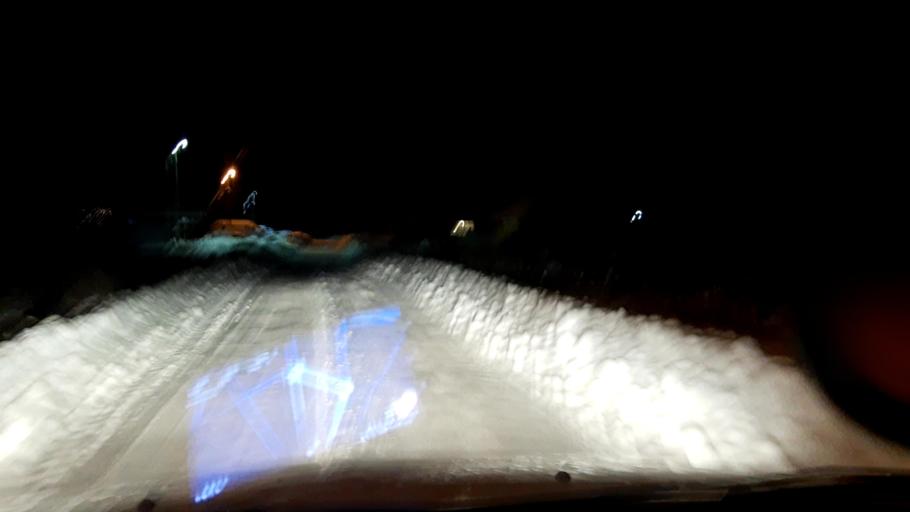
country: RU
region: Bashkortostan
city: Ufa
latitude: 54.6779
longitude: 56.1019
